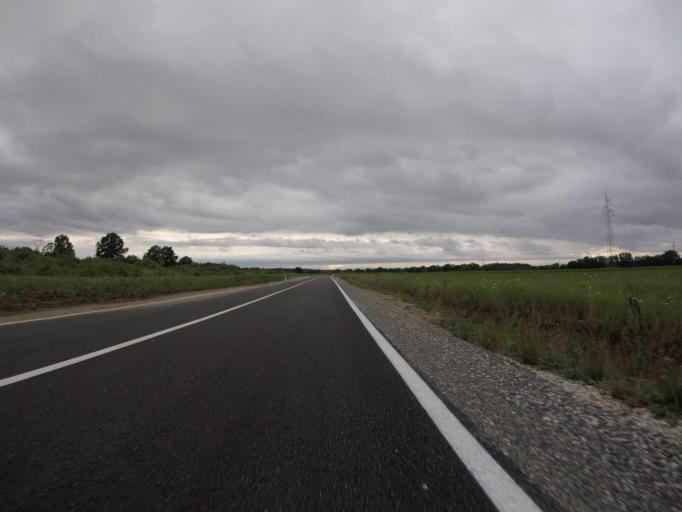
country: HR
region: Zagrebacka
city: Mraclin
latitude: 45.6571
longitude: 16.1037
